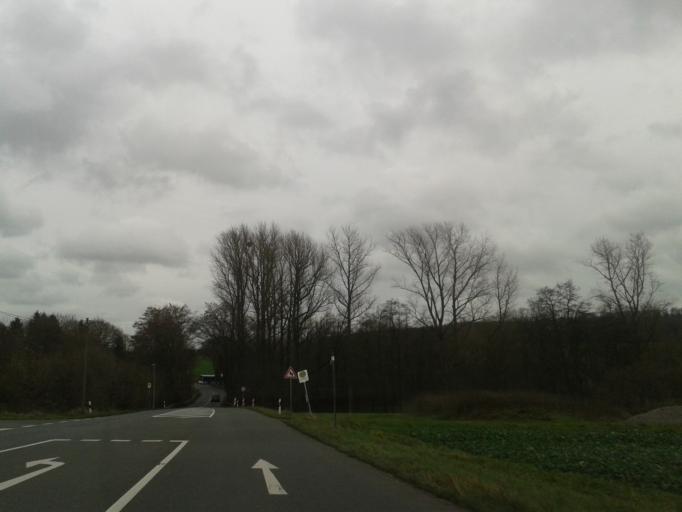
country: DE
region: North Rhine-Westphalia
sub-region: Regierungsbezirk Detmold
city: Blomberg
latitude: 51.9257
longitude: 9.1044
